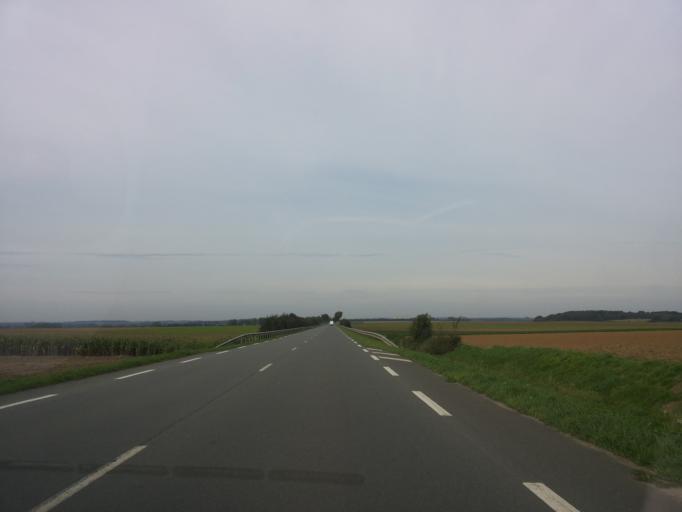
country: FR
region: Nord-Pas-de-Calais
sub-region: Departement du Pas-de-Calais
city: Bourlon
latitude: 50.2001
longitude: 3.1296
